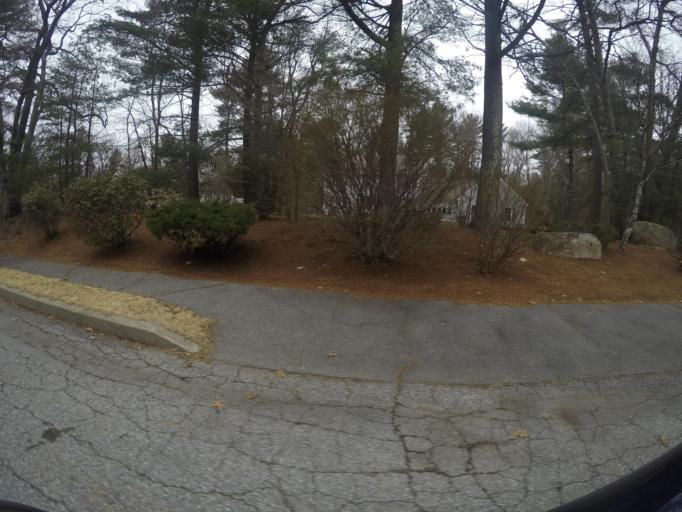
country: US
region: Massachusetts
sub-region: Bristol County
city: Easton
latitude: 42.0606
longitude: -71.1443
